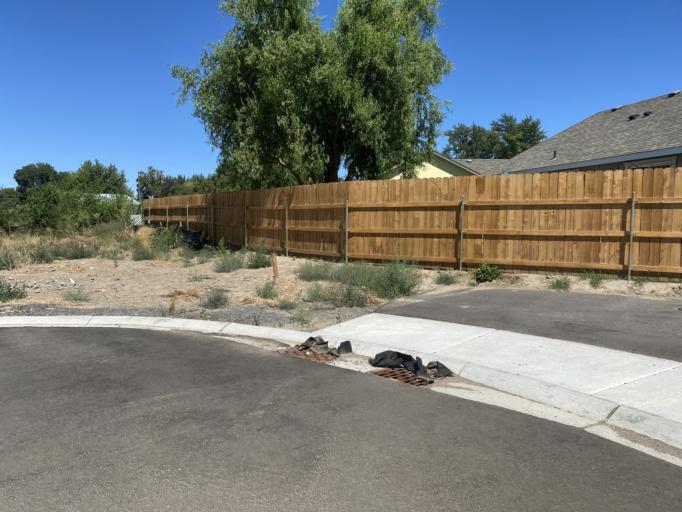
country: US
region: Washington
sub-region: Benton County
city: Kennewick
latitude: 46.2042
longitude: -119.1733
